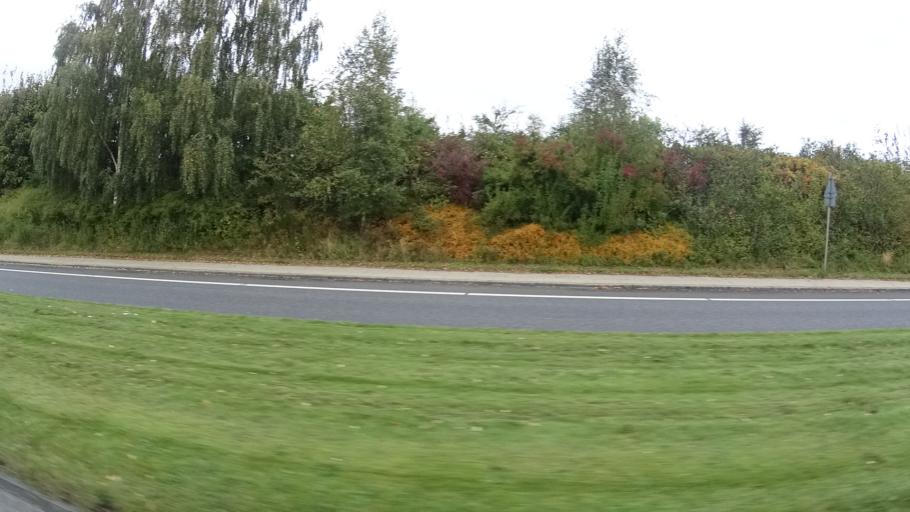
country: DK
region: South Denmark
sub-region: Vejle Kommune
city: Vejle
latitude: 55.6730
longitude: 9.5350
